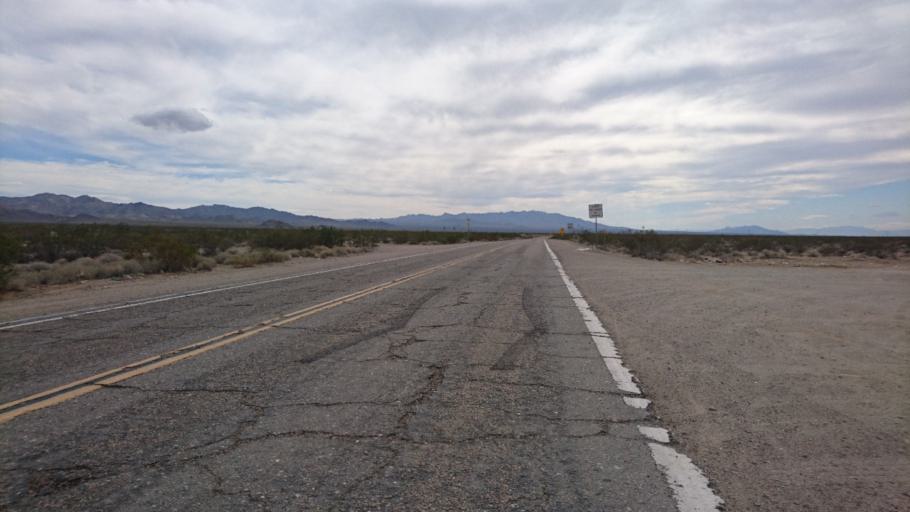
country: US
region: California
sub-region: San Bernardino County
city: Needles
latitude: 34.8107
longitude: -115.1905
